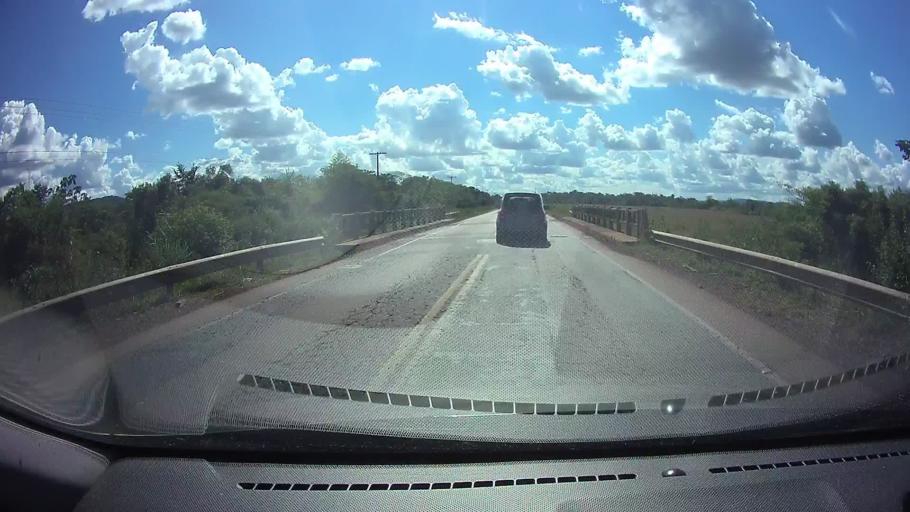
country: PY
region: Paraguari
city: La Colmena
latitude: -25.7527
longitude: -56.7799
